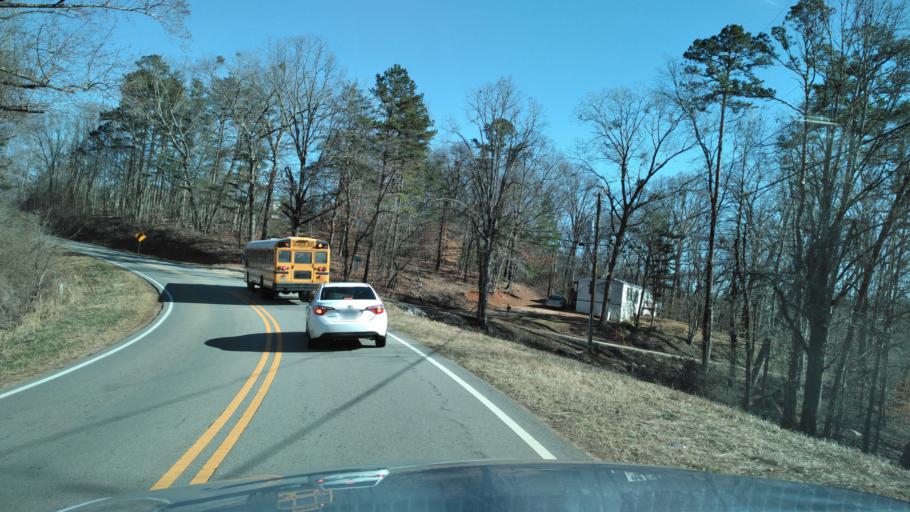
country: US
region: Georgia
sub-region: Hall County
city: Gainesville
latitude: 34.3159
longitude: -83.7541
